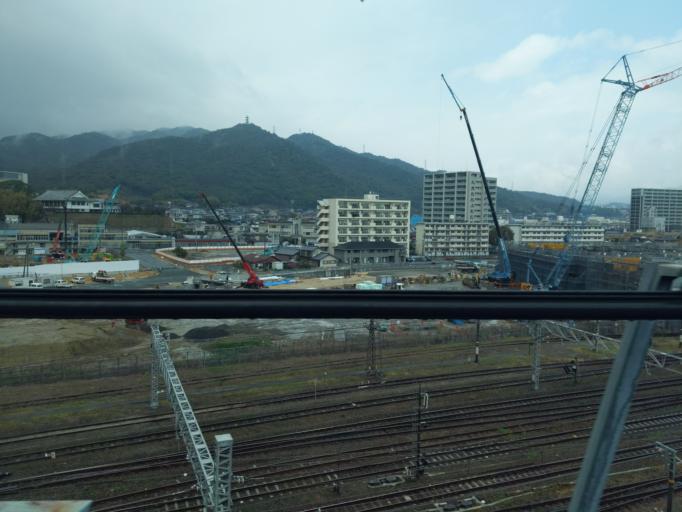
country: JP
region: Yamaguchi
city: Ogori-shimogo
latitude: 34.0916
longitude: 131.3943
